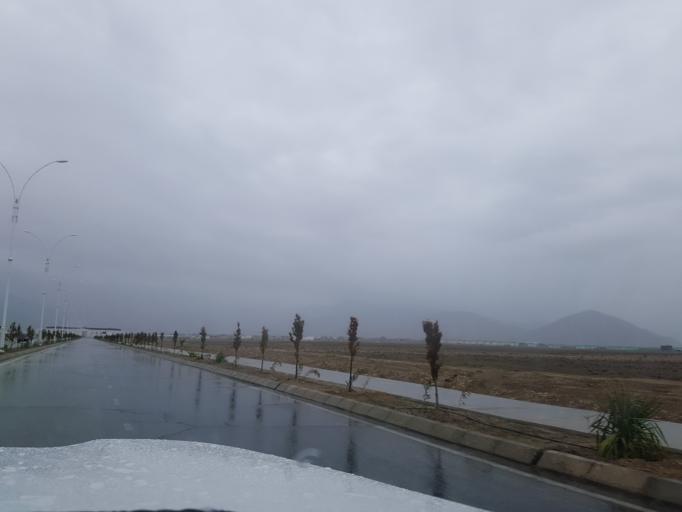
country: TM
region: Balkan
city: Balkanabat
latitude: 39.5551
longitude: 54.2929
